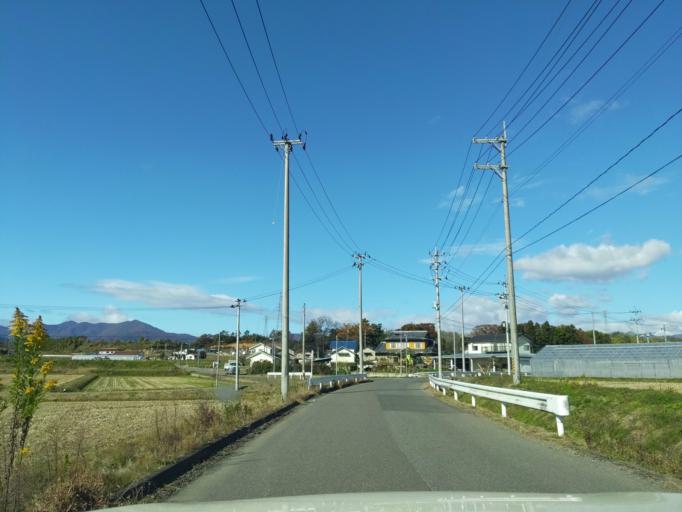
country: JP
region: Fukushima
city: Koriyama
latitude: 37.4423
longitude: 140.3264
